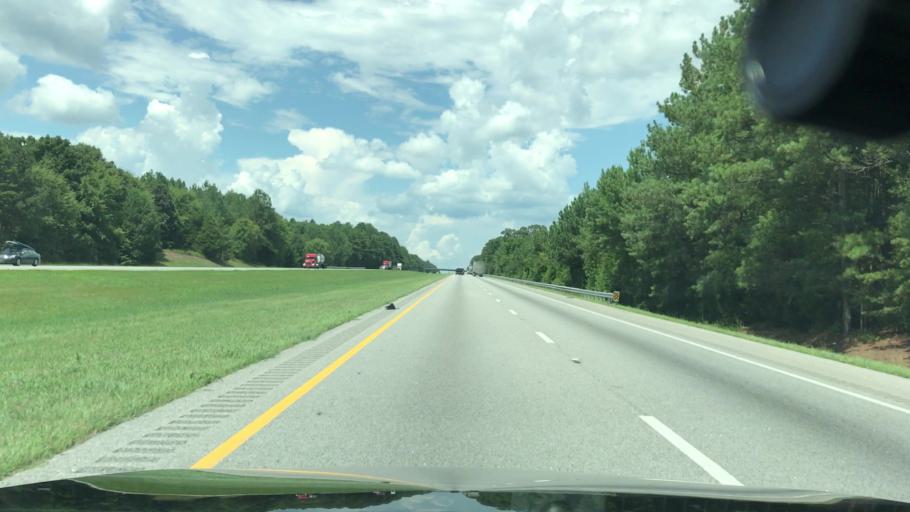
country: US
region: South Carolina
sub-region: Chester County
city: Great Falls
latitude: 34.6690
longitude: -81.0290
